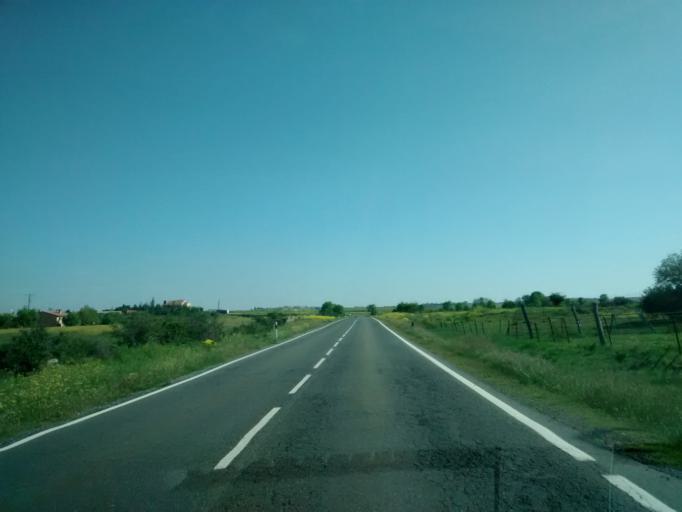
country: ES
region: Castille and Leon
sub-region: Provincia de Segovia
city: Trescasas
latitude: 40.9580
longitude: -4.0338
